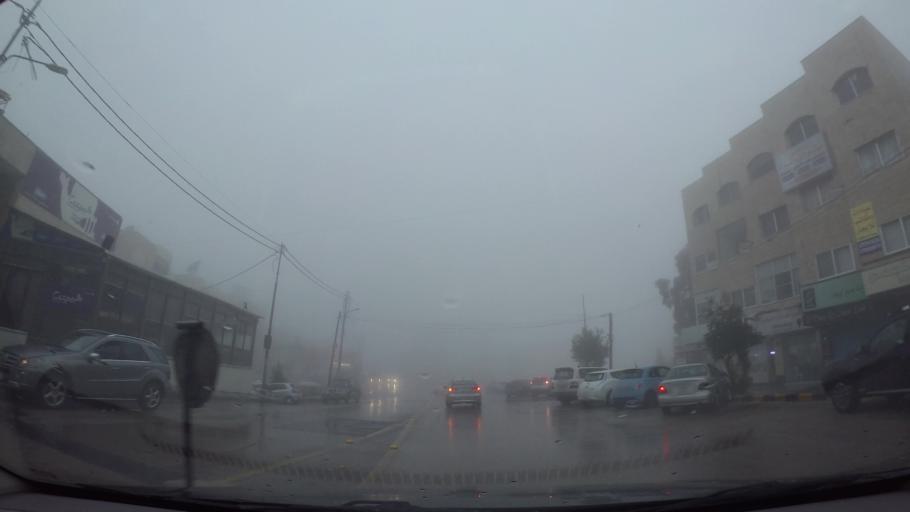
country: JO
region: Amman
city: Al Jubayhah
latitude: 32.0077
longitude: 35.8844
